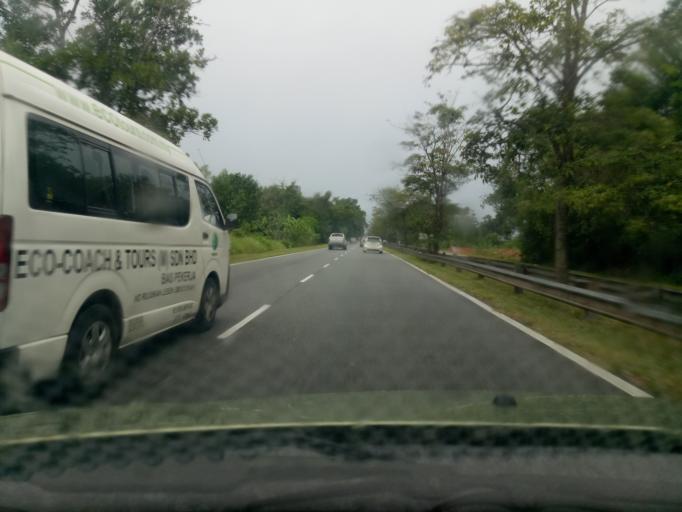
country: MY
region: Kedah
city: Sungai Petani
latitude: 5.6422
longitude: 100.5393
